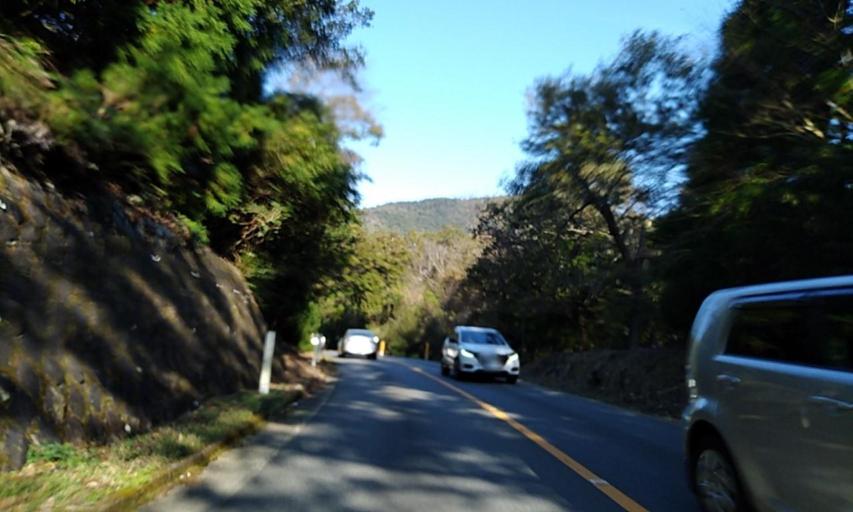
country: JP
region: Mie
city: Ise
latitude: 34.4537
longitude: 136.7425
